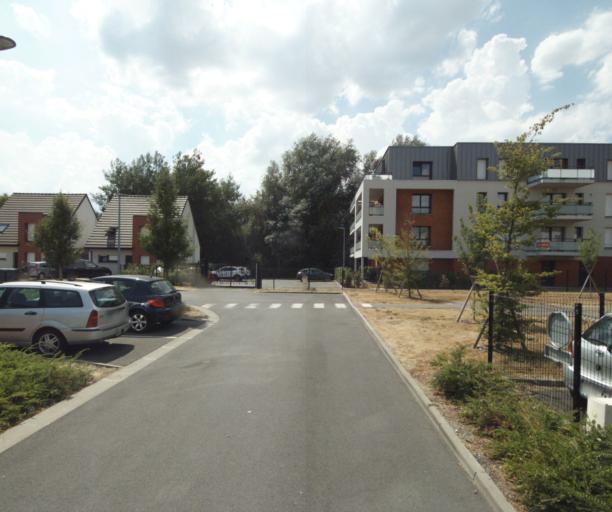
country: FR
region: Nord-Pas-de-Calais
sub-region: Departement du Nord
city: Comines
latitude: 50.7571
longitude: 2.9876
